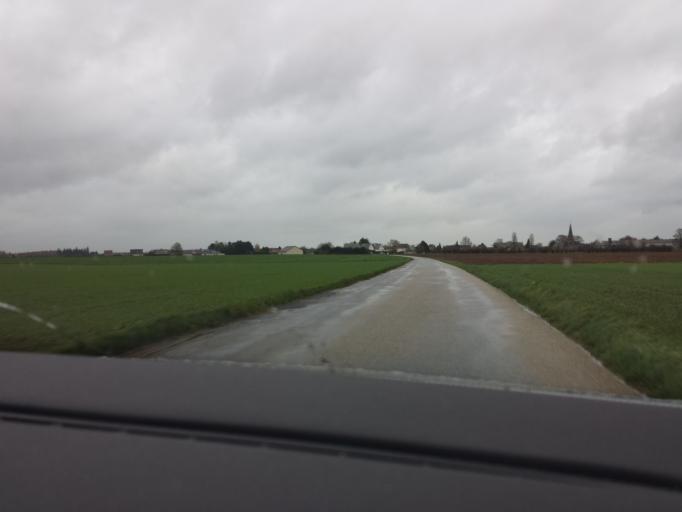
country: FR
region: Haute-Normandie
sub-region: Departement de l'Eure
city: Evreux
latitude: 49.0056
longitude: 1.2100
